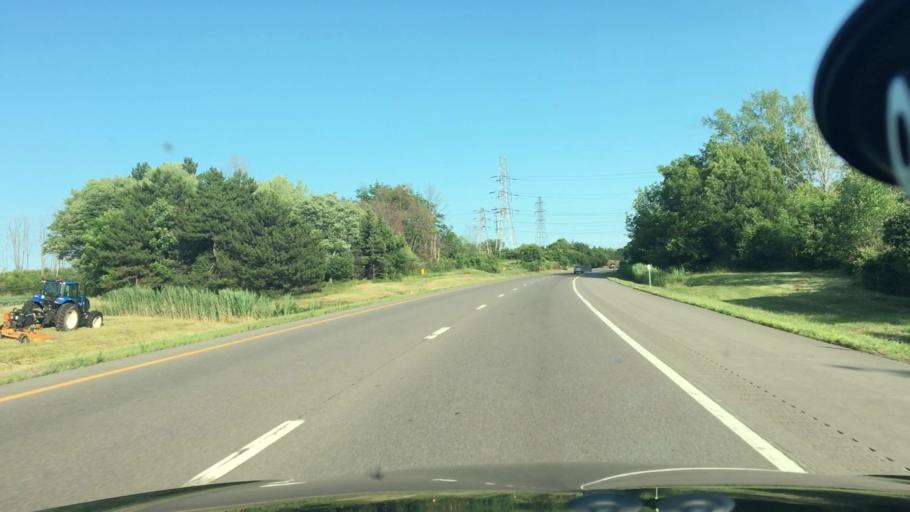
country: US
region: New York
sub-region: Erie County
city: Blasdell
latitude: 42.8084
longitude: -78.7852
